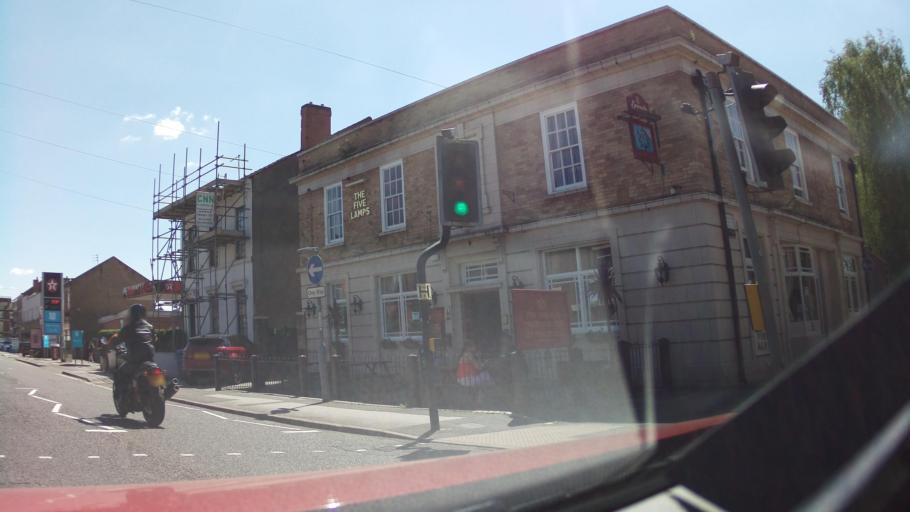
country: GB
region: England
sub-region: Derby
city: Derby
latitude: 52.9294
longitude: -1.4829
